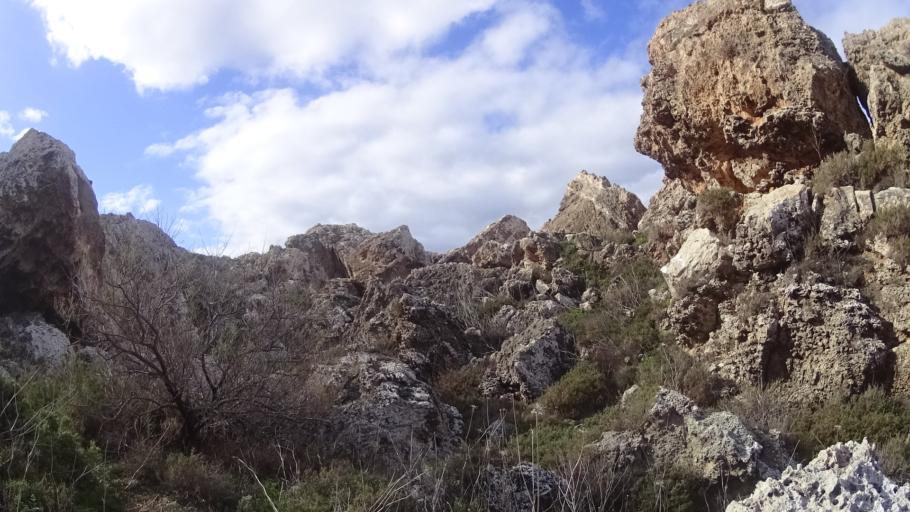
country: MT
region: Il-Mellieha
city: Mellieha
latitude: 35.9814
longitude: 14.3295
